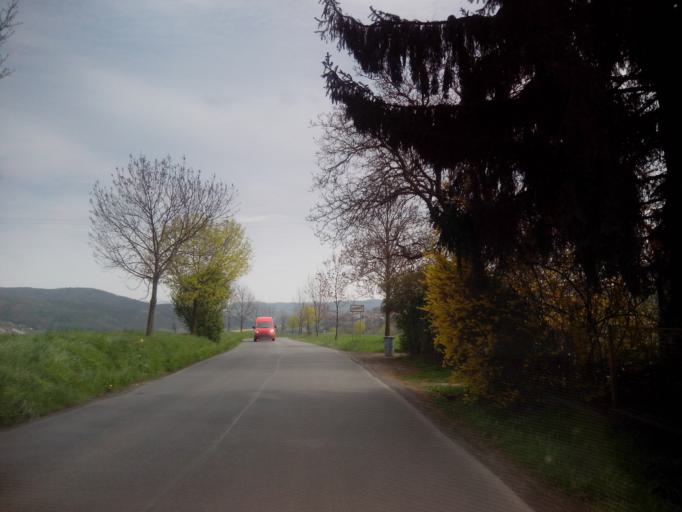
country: CZ
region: Central Bohemia
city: Hudlice
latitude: 49.9588
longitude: 13.9793
